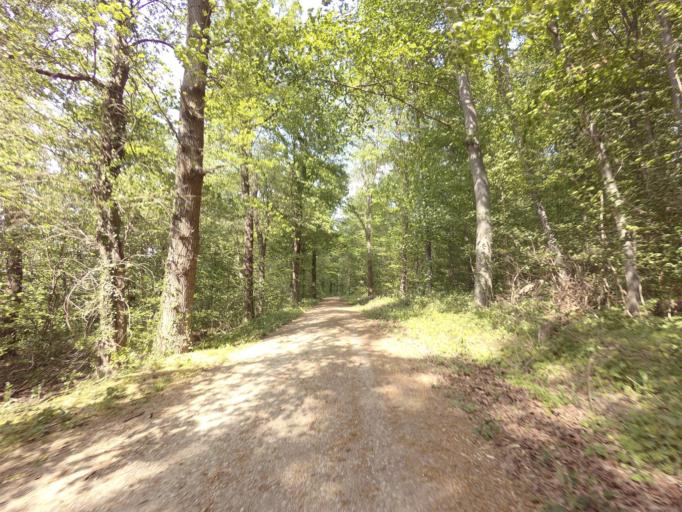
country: DE
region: Lower Saxony
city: Giesen
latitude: 52.1445
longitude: 9.8910
